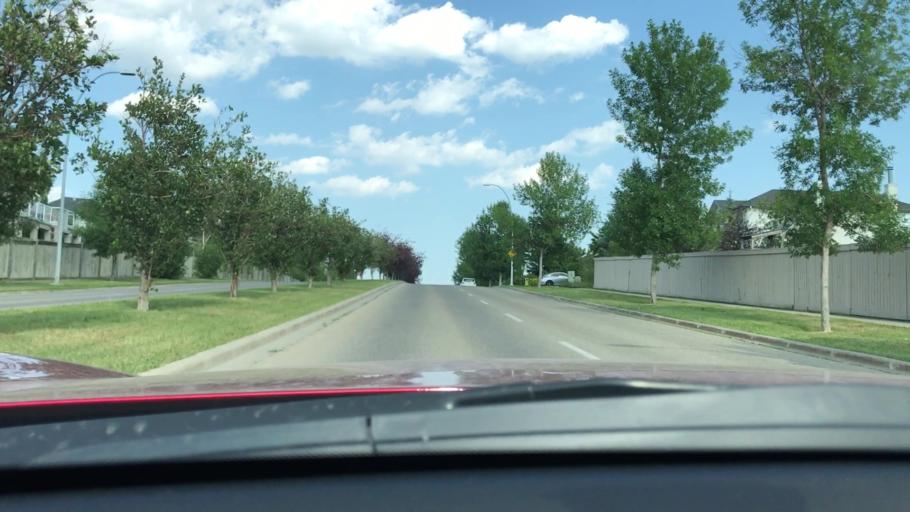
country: CA
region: Alberta
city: Calgary
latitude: 51.0305
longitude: -114.1800
